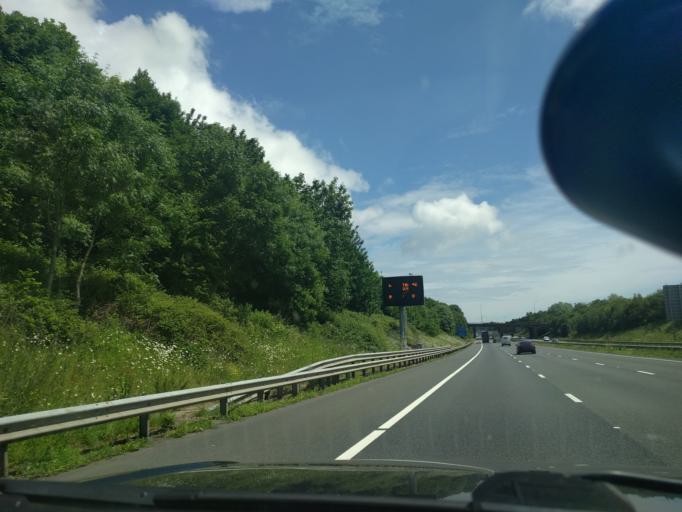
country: GB
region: Wales
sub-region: Newport
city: Marshfield
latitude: 51.5503
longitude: -3.0812
